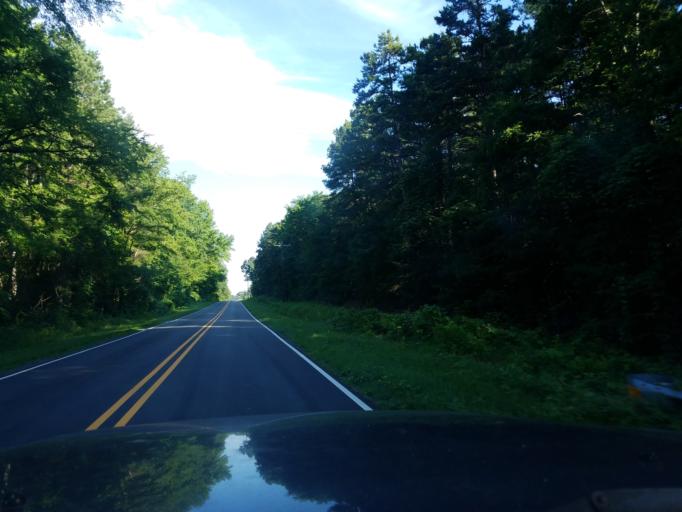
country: US
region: North Carolina
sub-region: Granville County
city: Butner
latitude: 36.1622
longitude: -78.7798
